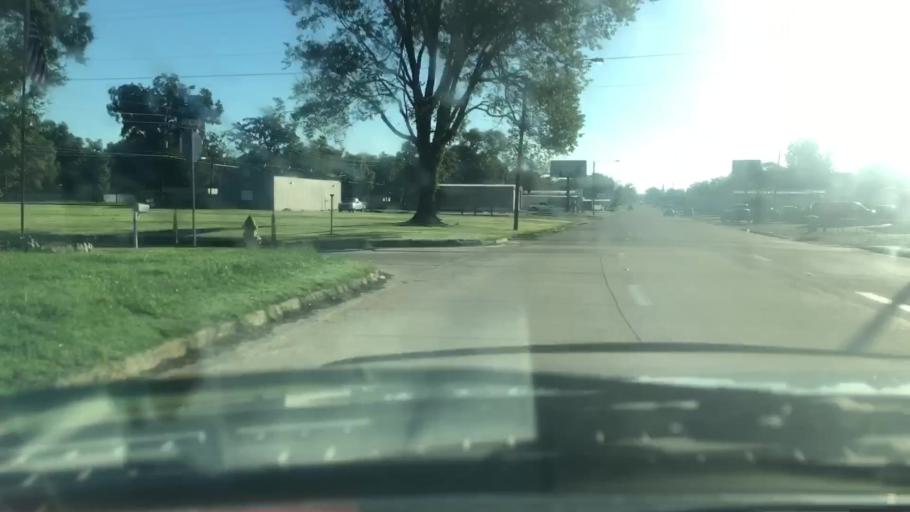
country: US
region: Texas
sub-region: Bowie County
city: Texarkana
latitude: 33.4232
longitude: -94.0695
